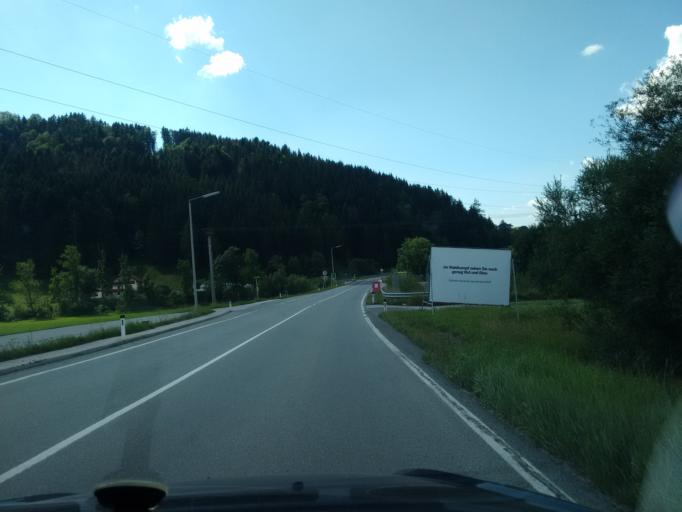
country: AT
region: Upper Austria
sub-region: Politischer Bezirk Kirchdorf an der Krems
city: Rossleithen
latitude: 47.7274
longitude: 14.2973
